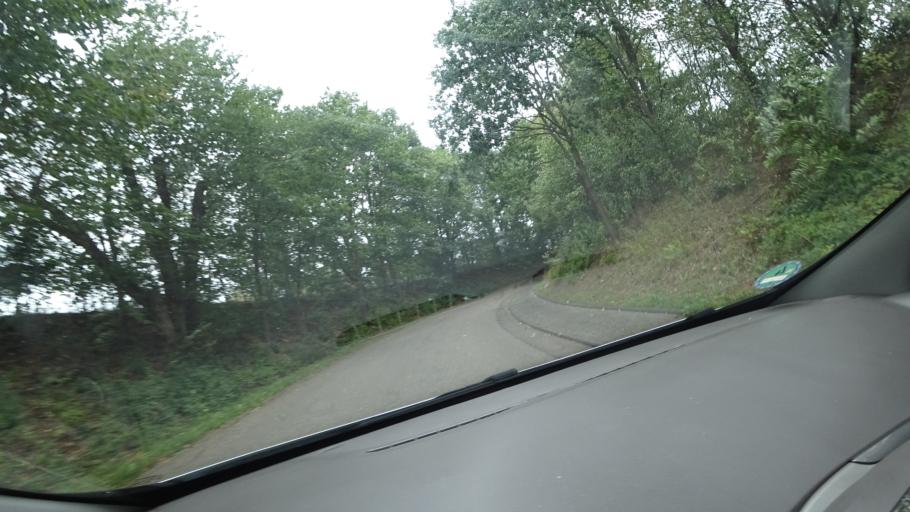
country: DE
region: Rheinland-Pfalz
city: Hohr-Grenzhausen
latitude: 50.4453
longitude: 7.6626
